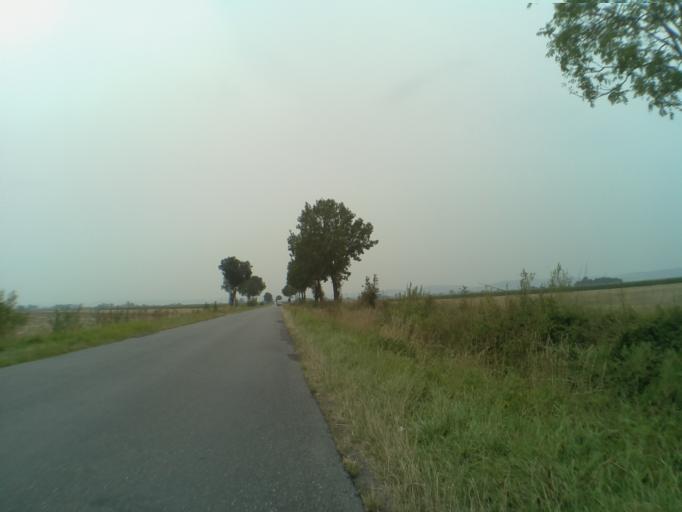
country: PL
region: Lower Silesian Voivodeship
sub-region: Powiat swidnicki
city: Strzegom
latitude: 50.9291
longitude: 16.3243
